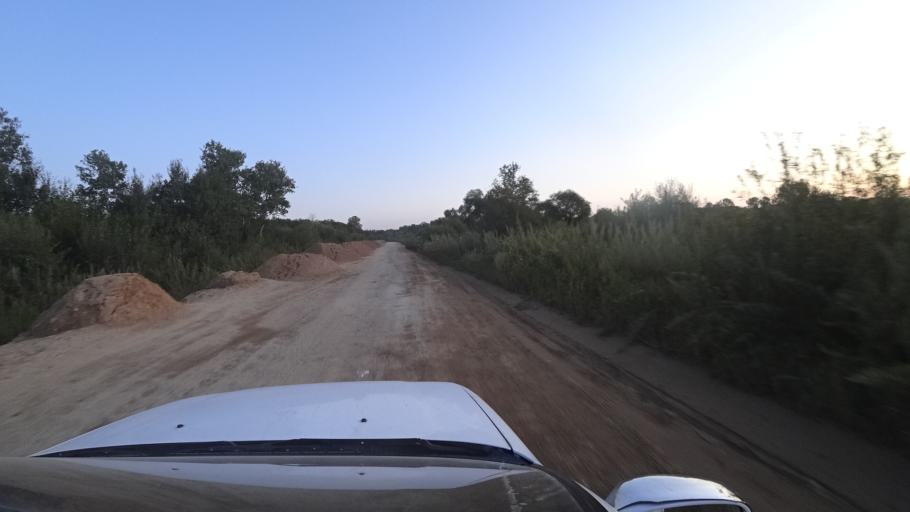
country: RU
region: Primorskiy
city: Dal'nerechensk
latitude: 45.9404
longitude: 133.7609
